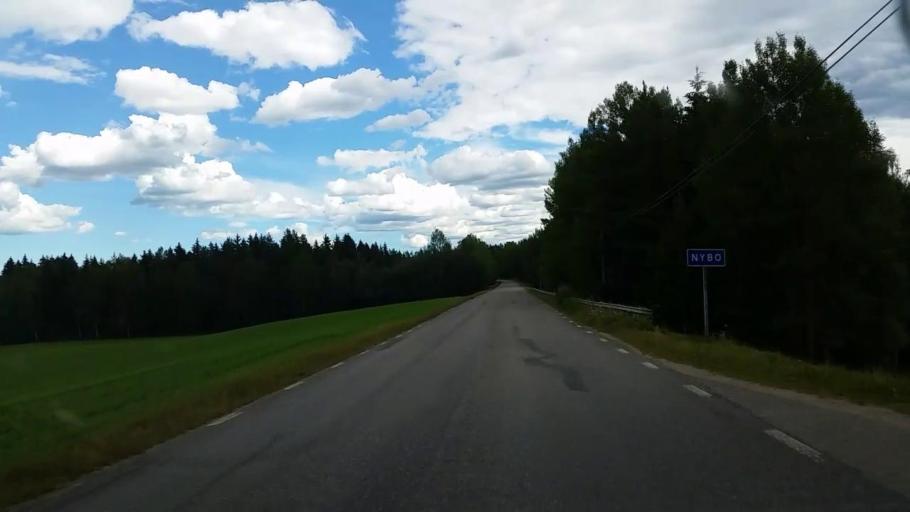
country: SE
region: Gaevleborg
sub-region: Ljusdals Kommun
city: Jaervsoe
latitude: 61.6713
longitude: 16.1265
